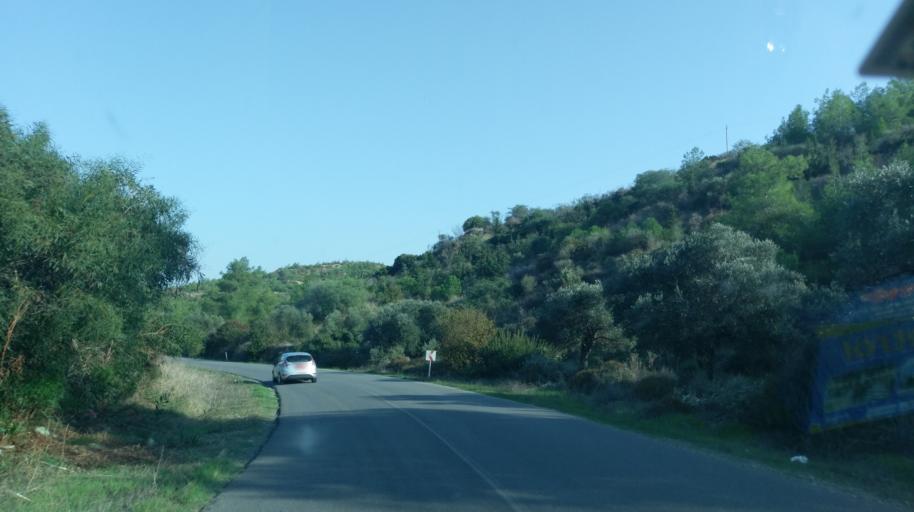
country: CY
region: Lefkosia
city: Lefka
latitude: 35.1517
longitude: 32.7816
